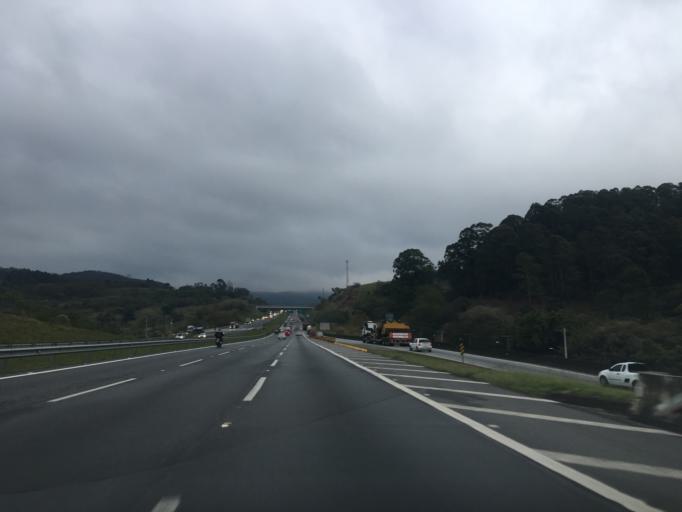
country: BR
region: Sao Paulo
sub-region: Caieiras
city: Caieiras
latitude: -23.4347
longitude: -46.7620
